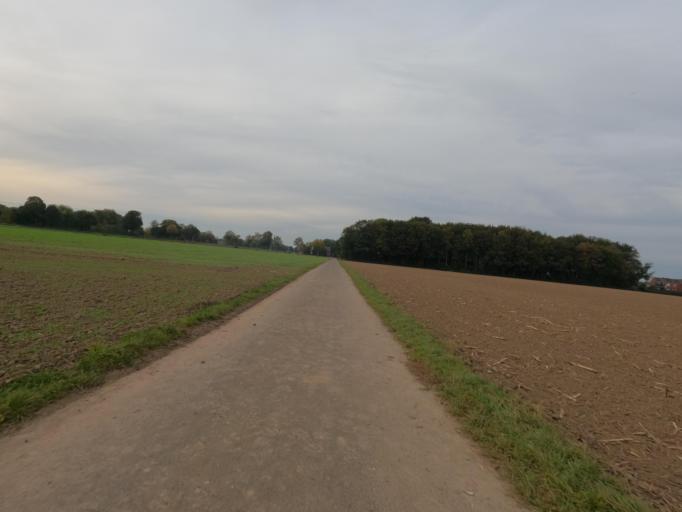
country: DE
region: North Rhine-Westphalia
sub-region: Regierungsbezirk Koln
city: Wassenberg
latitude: 51.0519
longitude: 6.1610
